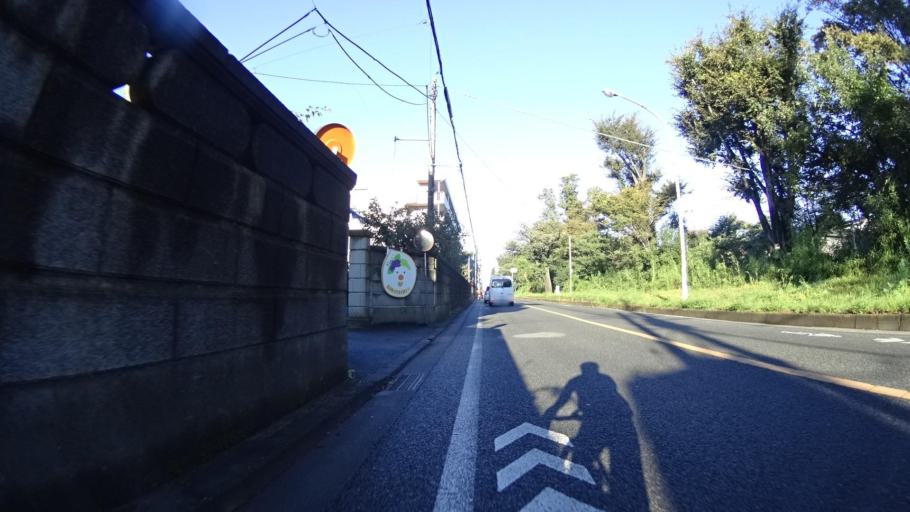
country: JP
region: Tokyo
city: Kokubunji
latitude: 35.7160
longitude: 139.4827
